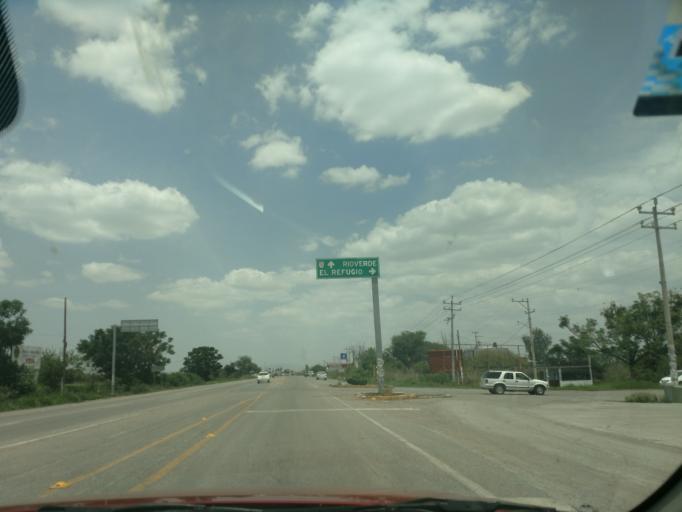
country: MX
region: San Luis Potosi
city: Ciudad Fernandez
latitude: 21.9419
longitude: -100.0421
